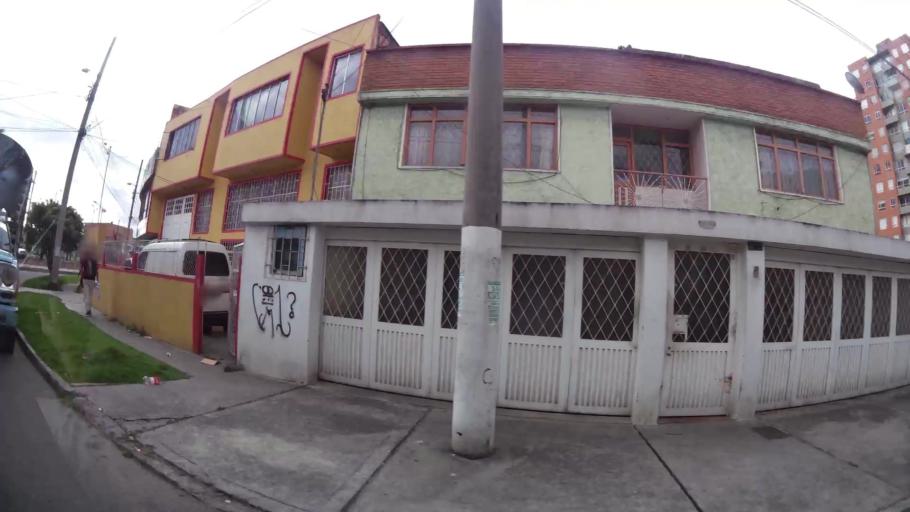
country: CO
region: Bogota D.C.
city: Bogota
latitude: 4.5977
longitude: -74.1418
